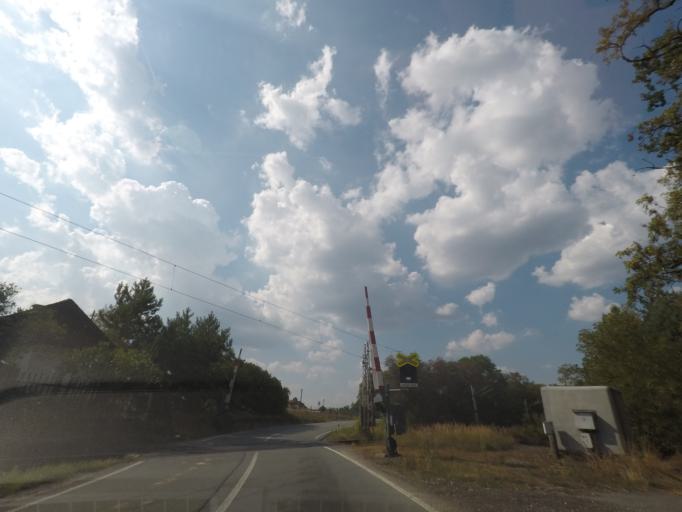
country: CZ
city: Albrechtice nad Orlici
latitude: 50.1299
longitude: 16.0635
